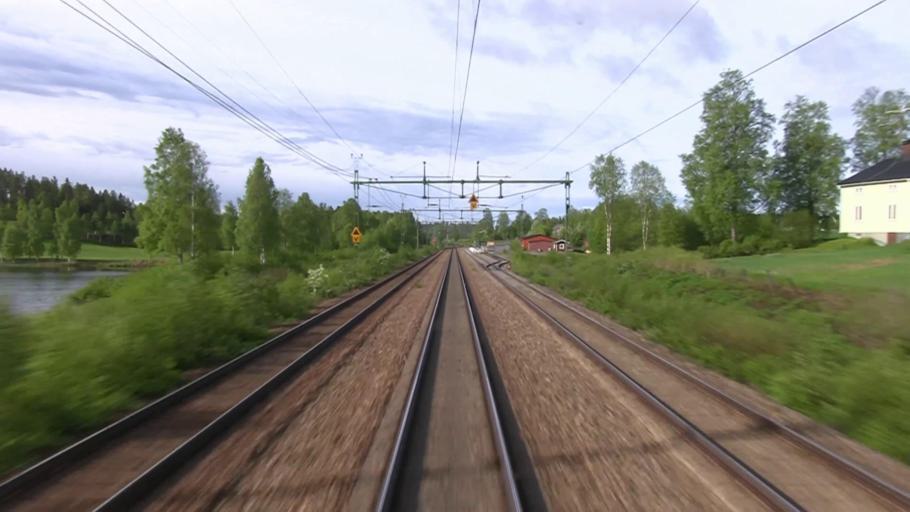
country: SE
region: Vaesterbotten
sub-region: Vindelns Kommun
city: Vindeln
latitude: 64.0997
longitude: 19.6777
